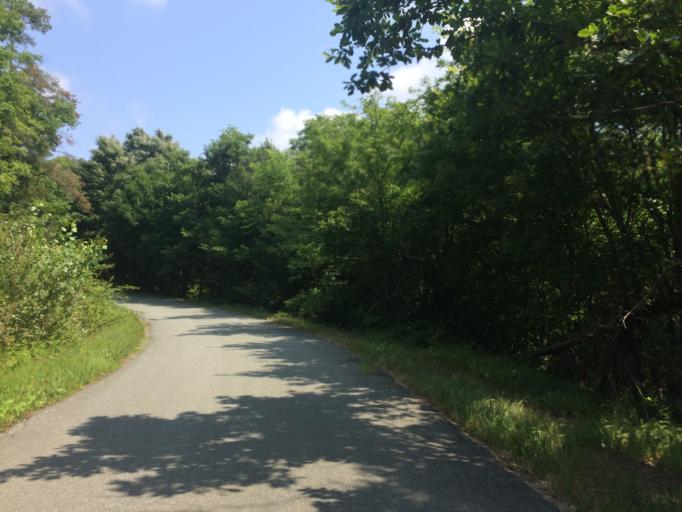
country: IT
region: Piedmont
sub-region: Provincia di Alessandria
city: Pareto
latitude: 44.4982
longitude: 8.3631
